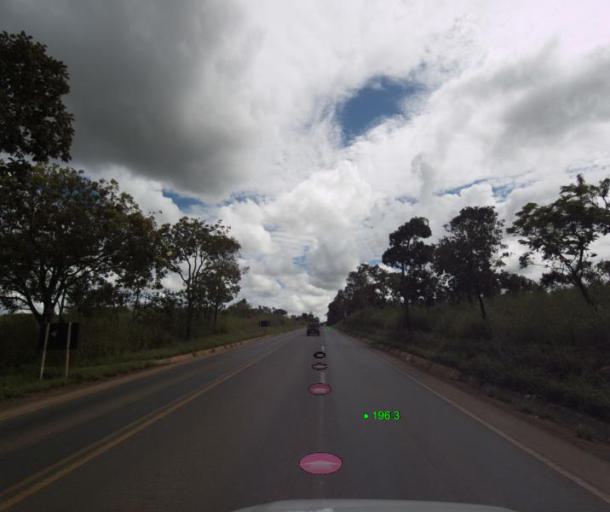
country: BR
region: Goias
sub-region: Uruacu
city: Uruacu
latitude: -14.4957
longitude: -49.1514
